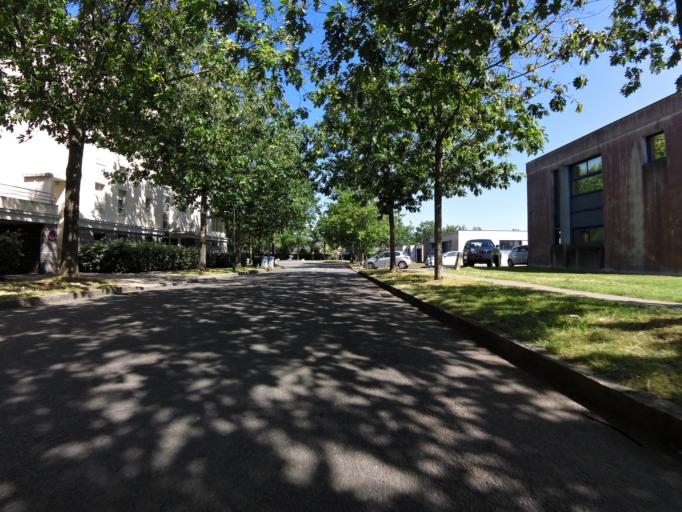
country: FR
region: Pays de la Loire
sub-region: Departement de la Loire-Atlantique
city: Saint-Herblain
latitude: 47.2276
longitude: -1.6089
